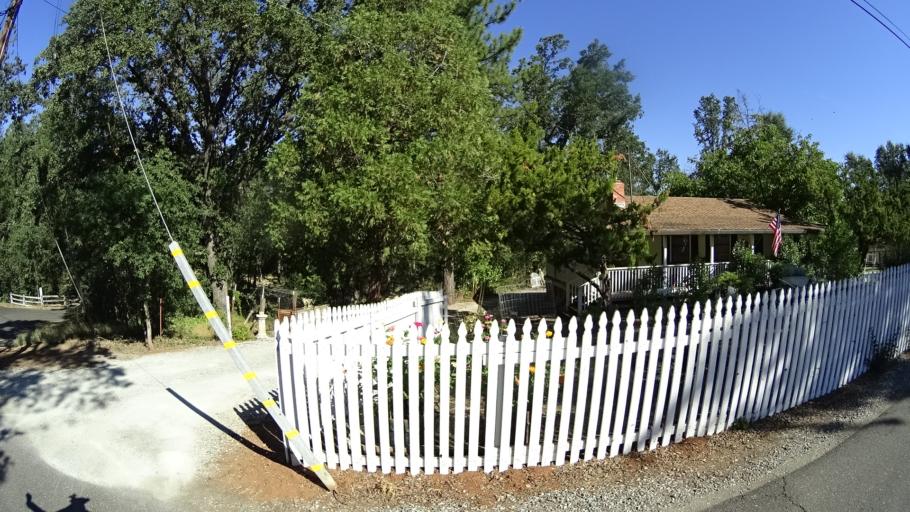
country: US
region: California
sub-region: Calaveras County
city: Murphys
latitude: 38.1343
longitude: -120.4619
